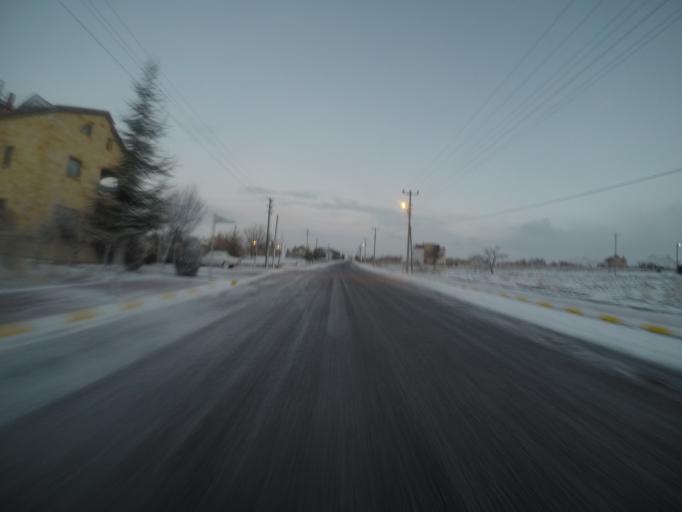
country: TR
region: Nevsehir
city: Goereme
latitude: 38.6222
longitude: 34.8008
